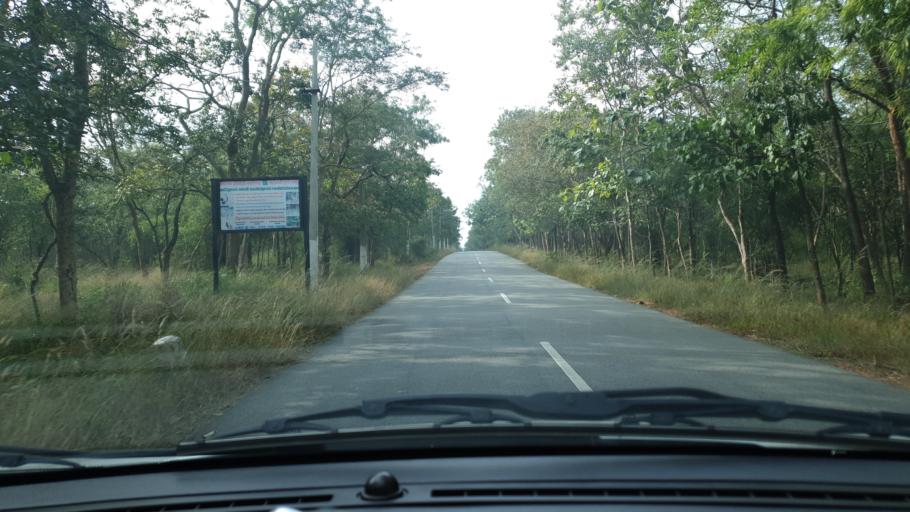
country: IN
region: Andhra Pradesh
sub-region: Kurnool
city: Srisailam
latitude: 16.2885
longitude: 78.7291
